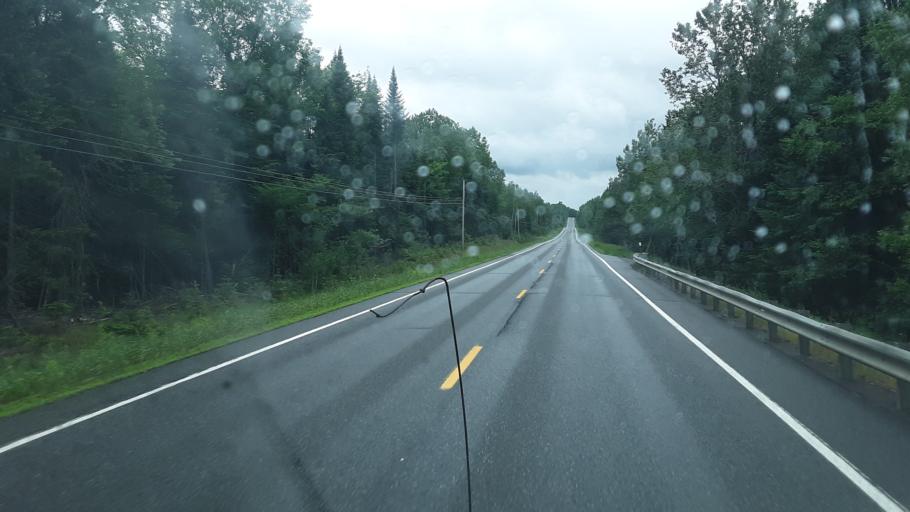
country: US
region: Maine
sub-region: Aroostook County
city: Presque Isle
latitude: 46.4570
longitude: -68.3850
